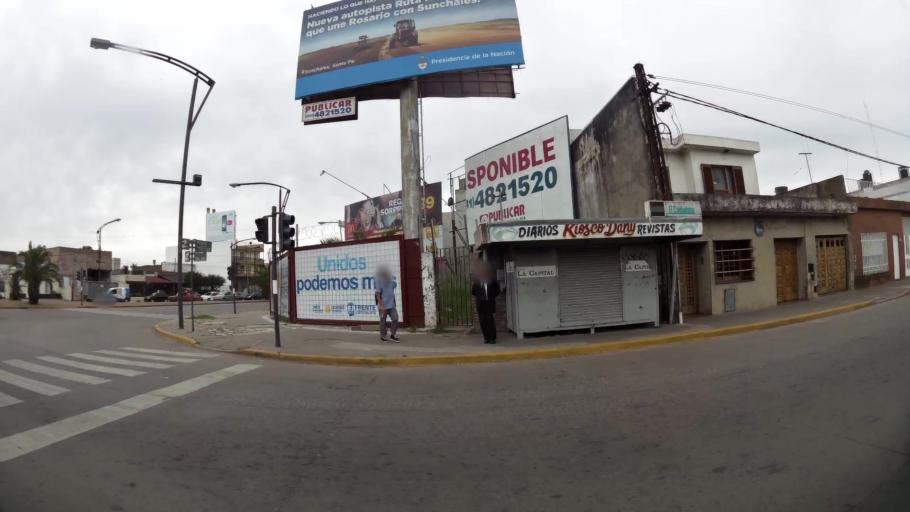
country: AR
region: Santa Fe
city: Gobernador Galvez
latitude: -32.9913
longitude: -60.6649
